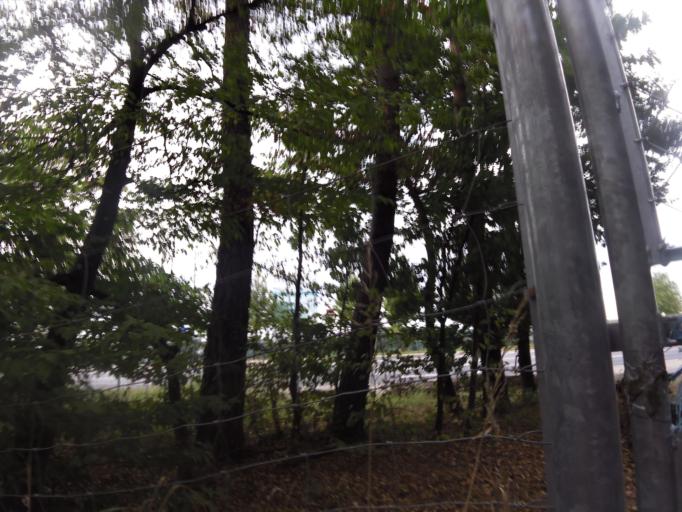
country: DE
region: Hesse
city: Morfelden-Walldorf
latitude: 50.0225
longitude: 8.5572
